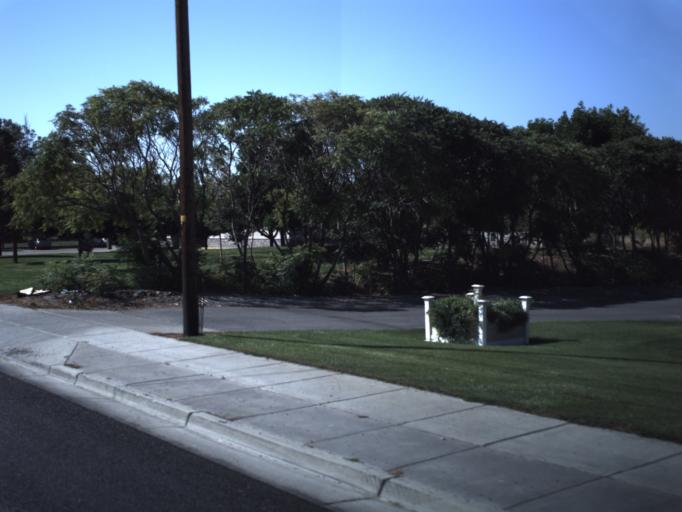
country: US
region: Utah
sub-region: Cache County
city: Nibley
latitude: 41.6825
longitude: -111.8338
